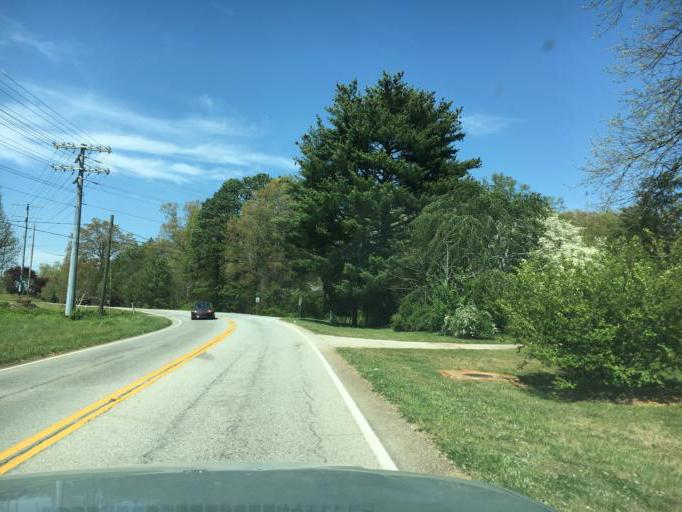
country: US
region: South Carolina
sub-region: Greenville County
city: Greer
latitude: 34.9630
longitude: -82.2260
